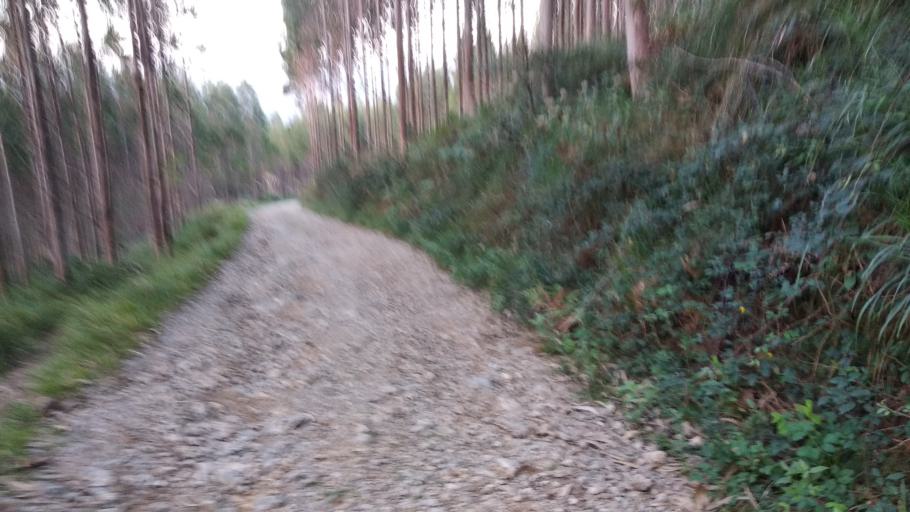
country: ES
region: Cantabria
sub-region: Provincia de Cantabria
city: Entrambasaguas
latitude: 43.3278
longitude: -3.6845
